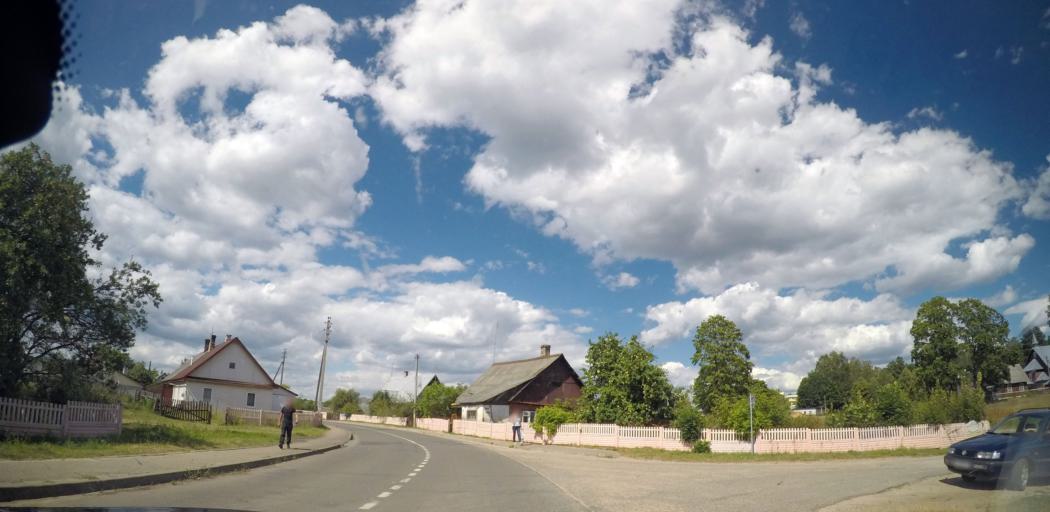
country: LT
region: Alytaus apskritis
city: Druskininkai
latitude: 53.8825
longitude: 24.1393
